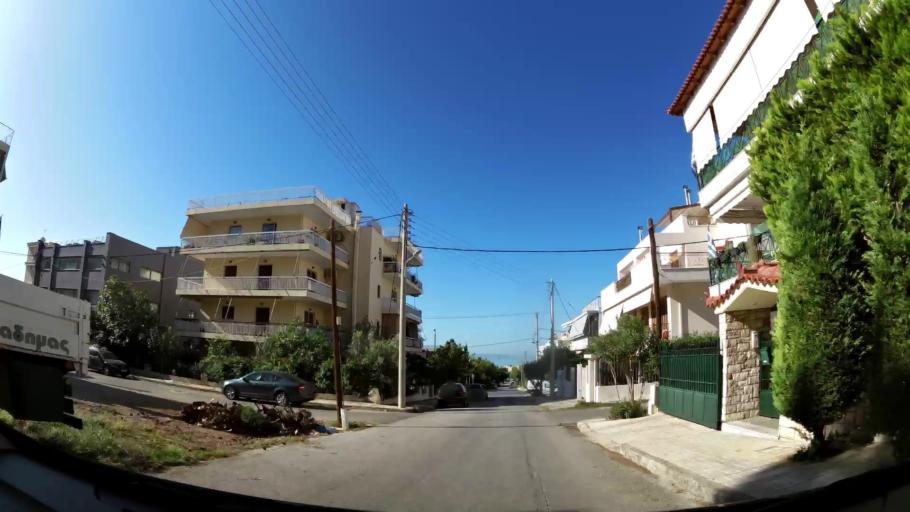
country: GR
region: Attica
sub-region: Nomarchia Athinas
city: Glyfada
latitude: 37.8697
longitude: 23.7666
